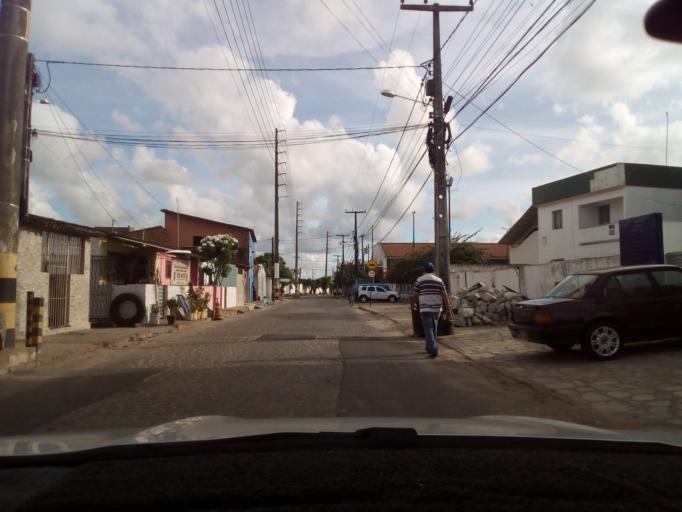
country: BR
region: Paraiba
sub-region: Joao Pessoa
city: Joao Pessoa
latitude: -7.1650
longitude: -34.8808
